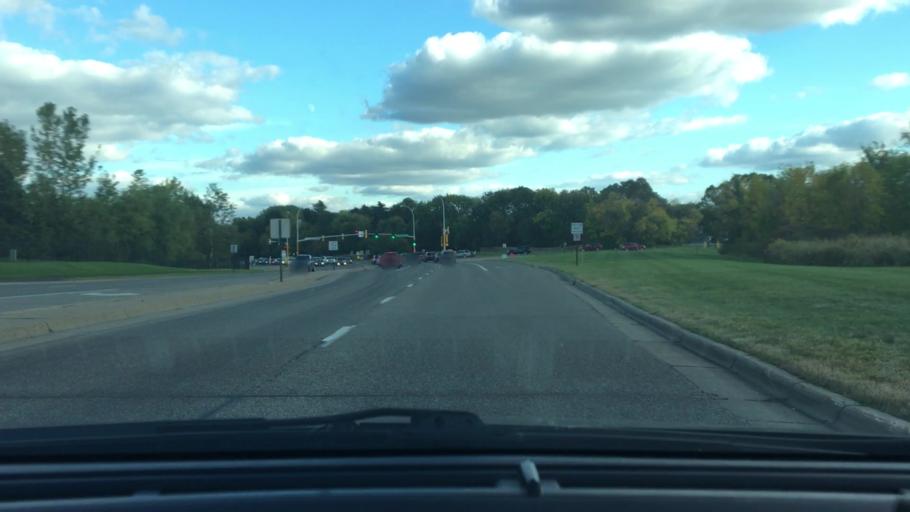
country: US
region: Minnesota
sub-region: Hennepin County
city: Maple Grove
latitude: 45.0639
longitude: -93.4402
